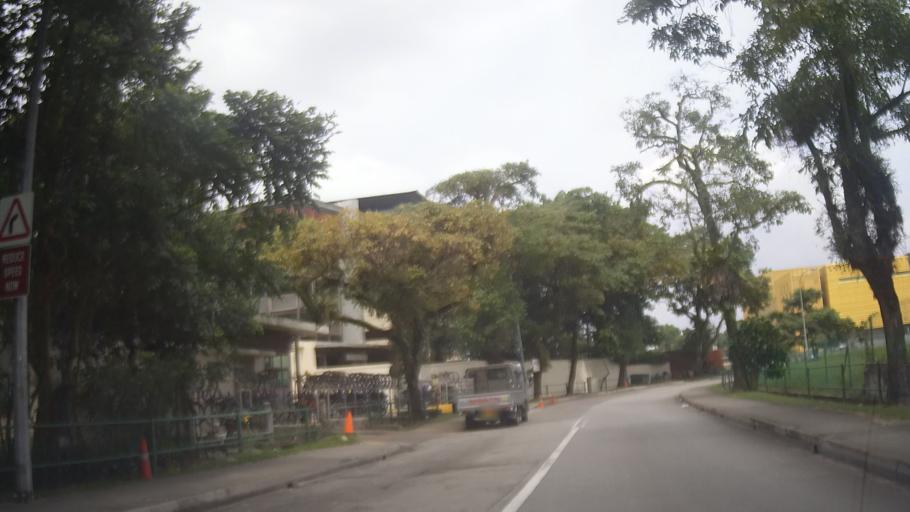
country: MY
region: Johor
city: Johor Bahru
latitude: 1.4133
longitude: 103.7472
